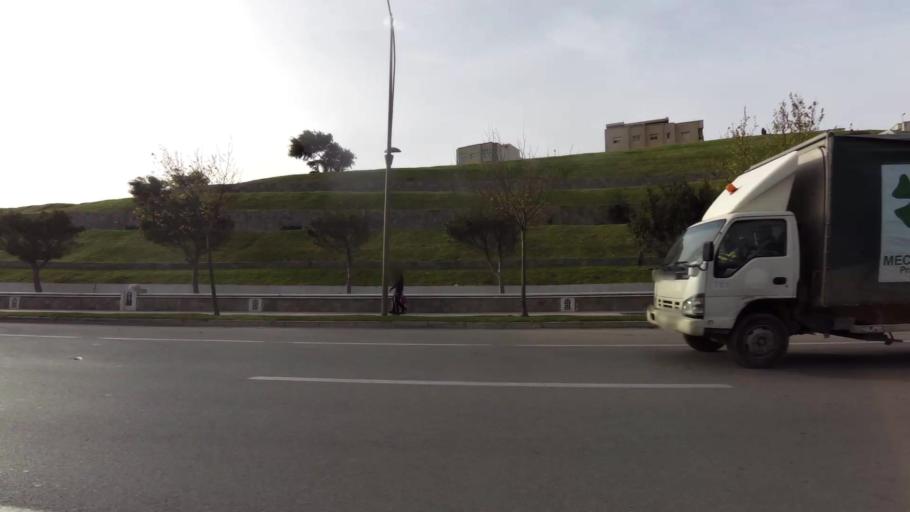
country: MA
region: Tanger-Tetouan
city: Tetouan
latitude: 35.5666
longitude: -5.4094
